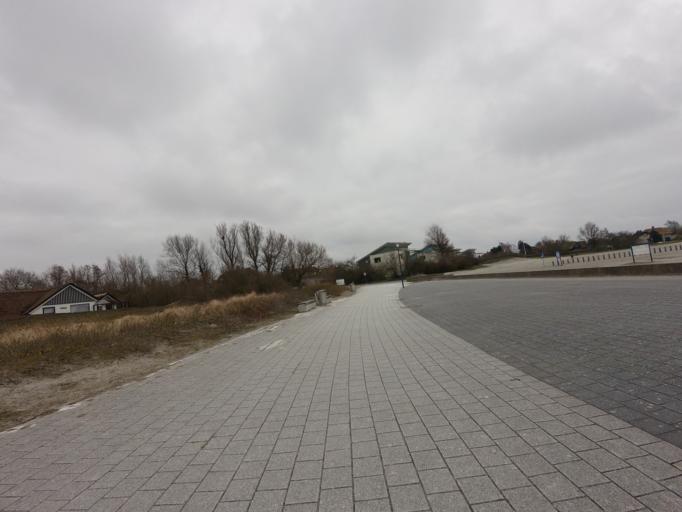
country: NL
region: Friesland
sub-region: Sudwest Fryslan
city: Makkum
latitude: 53.0482
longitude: 5.3810
